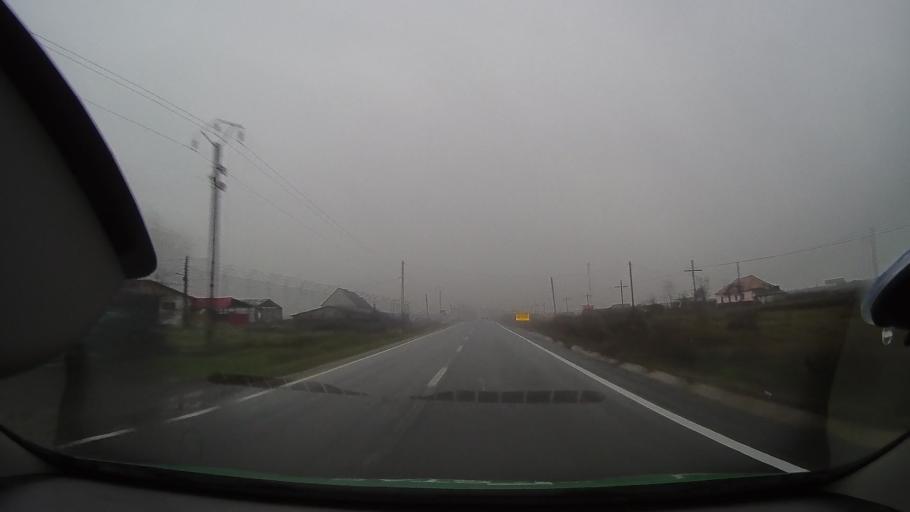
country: RO
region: Bihor
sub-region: Comuna Olcea
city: Olcea
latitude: 46.6899
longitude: 21.9656
